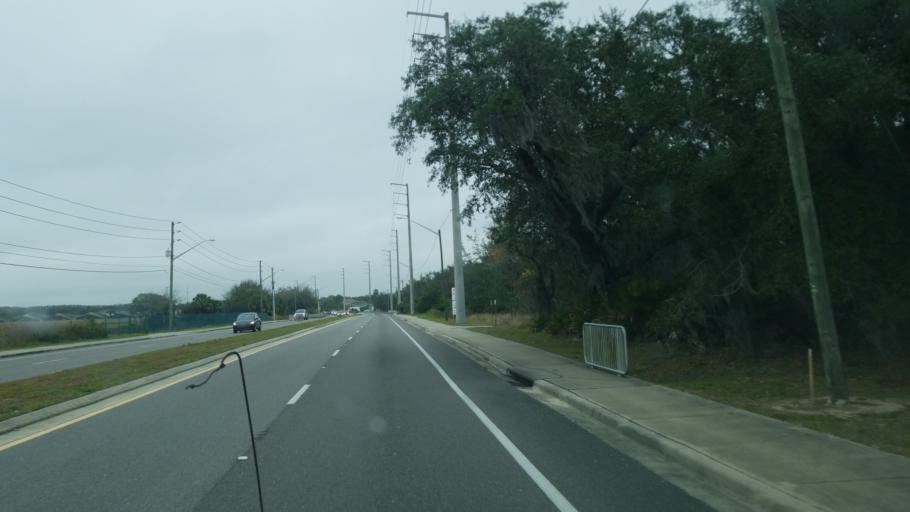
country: US
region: Florida
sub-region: Polk County
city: Loughman
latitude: 28.2576
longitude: -81.6354
